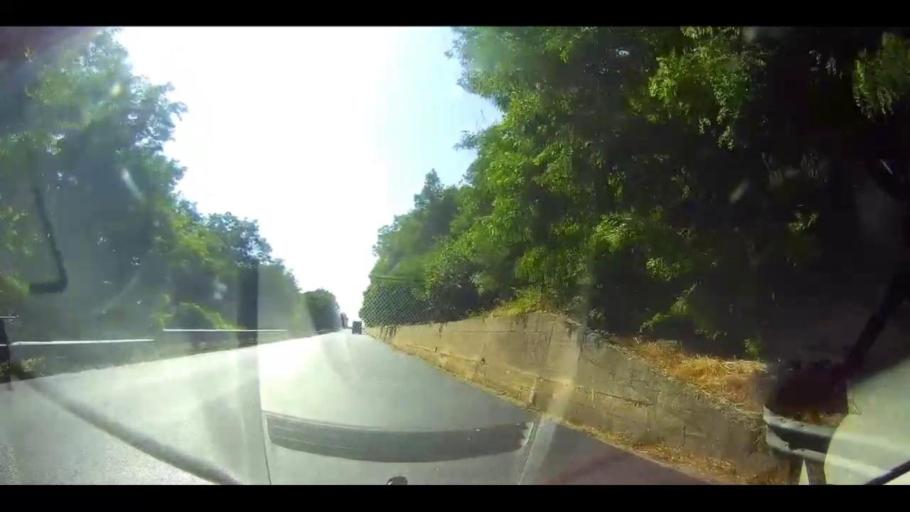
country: IT
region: Calabria
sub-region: Provincia di Cosenza
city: Celico
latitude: 39.3184
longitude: 16.3678
